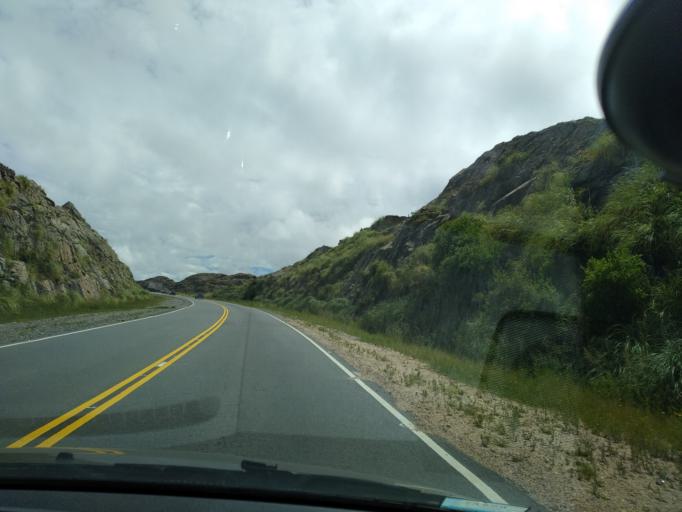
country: AR
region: Cordoba
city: Mina Clavero
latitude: -31.6994
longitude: -64.8946
